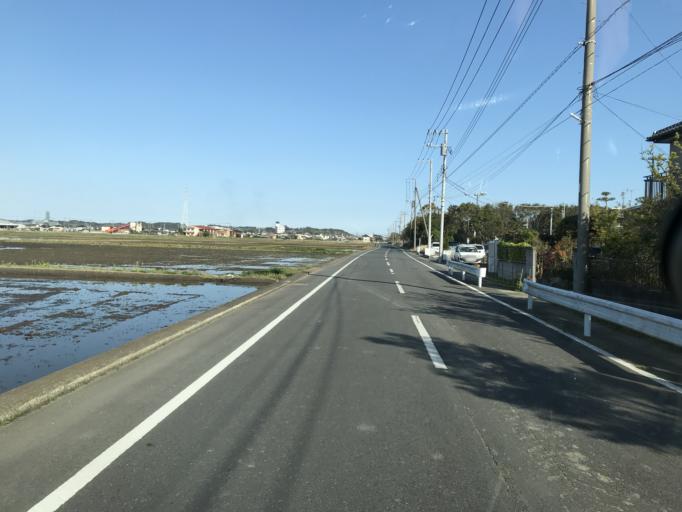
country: JP
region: Chiba
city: Omigawa
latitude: 35.8444
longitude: 140.6146
